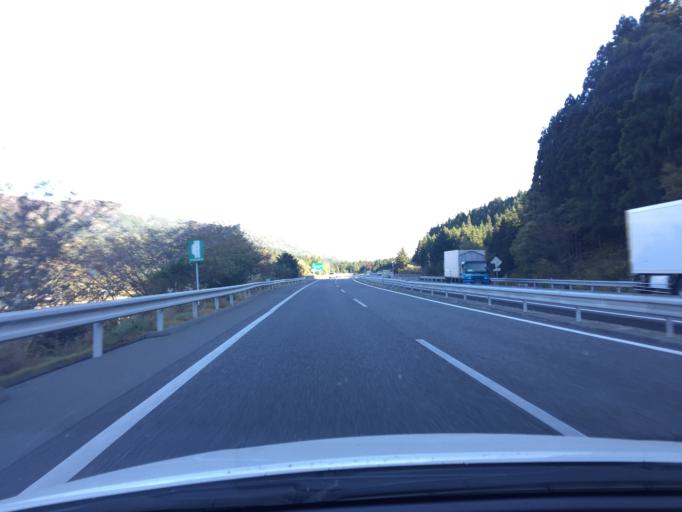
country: JP
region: Fukushima
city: Iwaki
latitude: 37.1077
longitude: 140.7623
